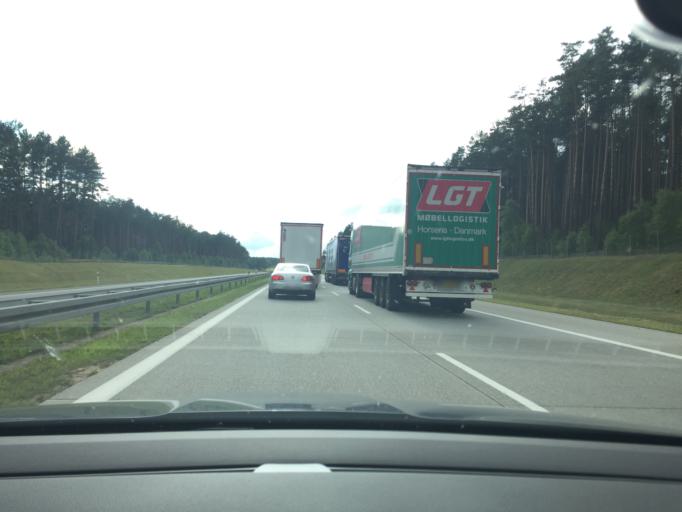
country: PL
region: Lubusz
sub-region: Powiat sulecinski
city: Torzym
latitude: 52.3261
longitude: 15.1202
